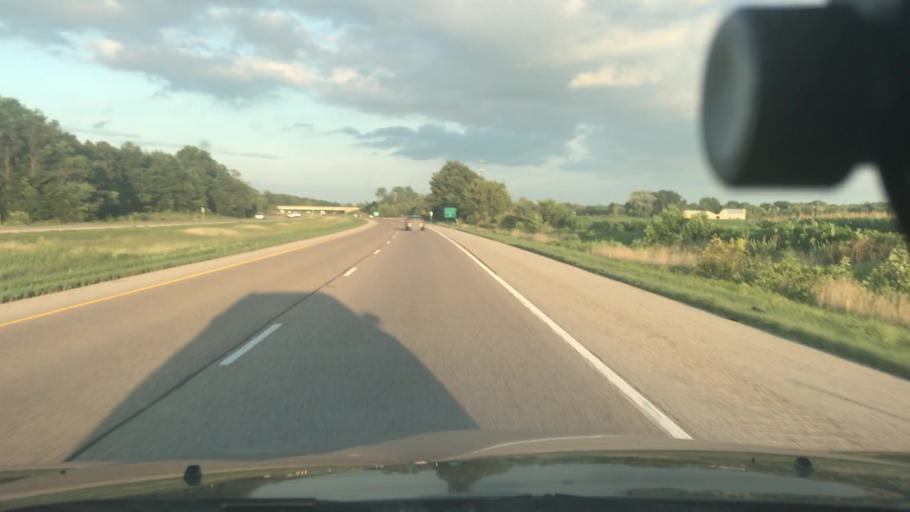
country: US
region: Illinois
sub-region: Clinton County
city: Albers
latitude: 38.5029
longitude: -89.6197
